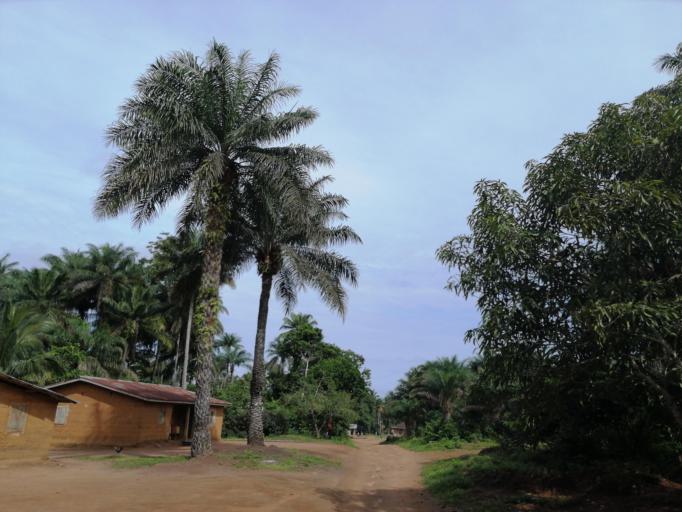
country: SL
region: Northern Province
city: Port Loko
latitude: 8.7892
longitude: -12.9273
